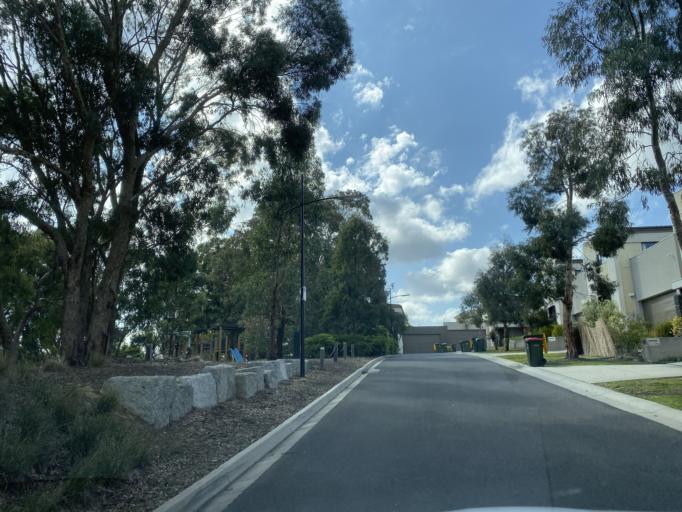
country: AU
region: Victoria
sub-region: Whitehorse
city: Burwood
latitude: -37.8485
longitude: 145.1251
